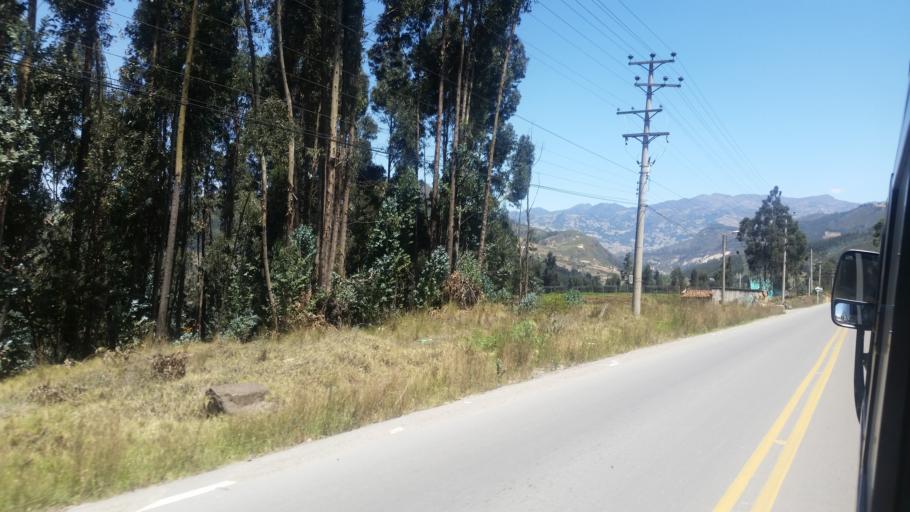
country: CO
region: Boyaca
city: Mongui
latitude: 5.7647
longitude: -72.8782
